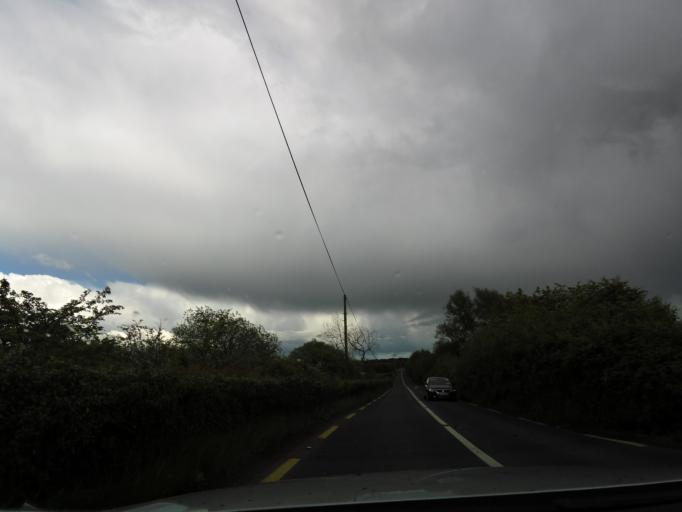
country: IE
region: Munster
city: Thurles
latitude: 52.7213
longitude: -7.8309
